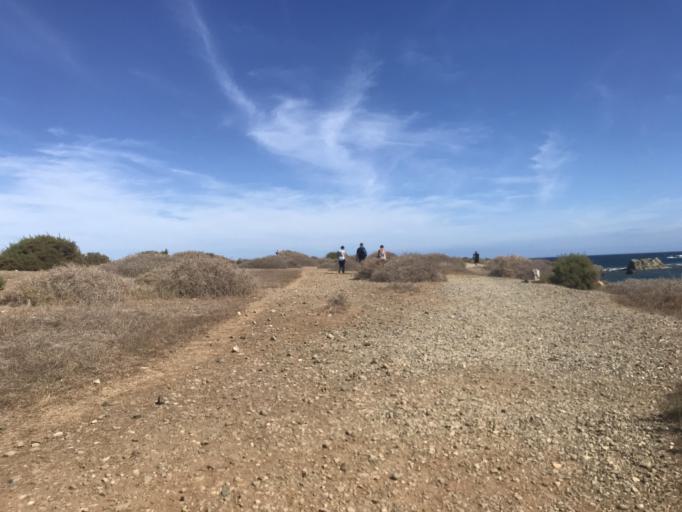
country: ES
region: Valencia
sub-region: Provincia de Alicante
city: Santa Pola
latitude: 38.1630
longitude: -0.4693
